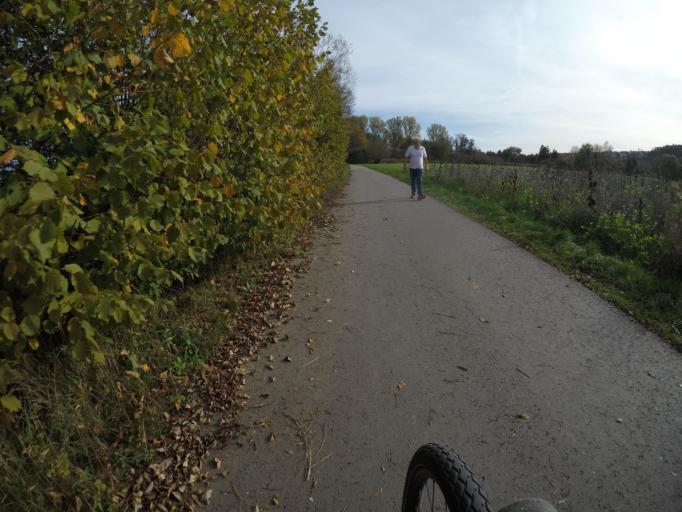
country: DE
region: Baden-Wuerttemberg
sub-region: Regierungsbezirk Stuttgart
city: Weil der Stadt
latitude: 48.7640
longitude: 8.8613
